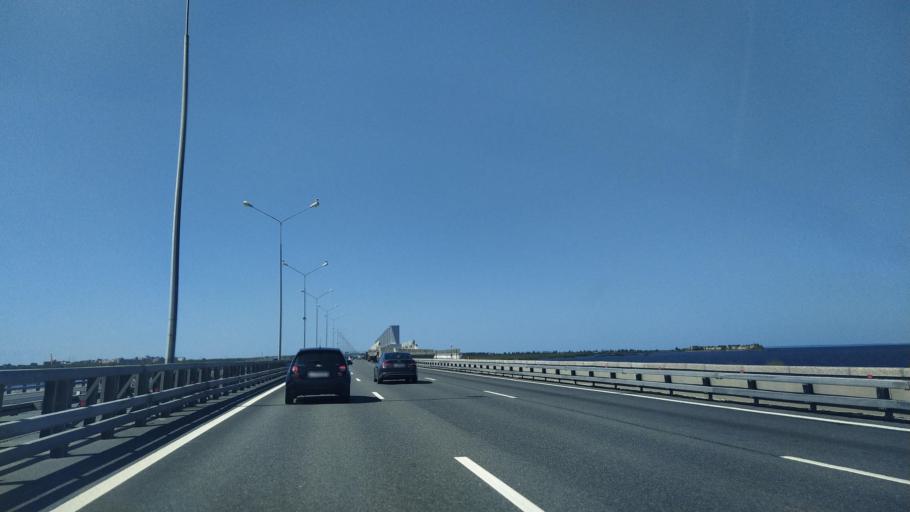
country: RU
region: St.-Petersburg
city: Kronshtadt
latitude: 60.0219
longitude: 29.7881
